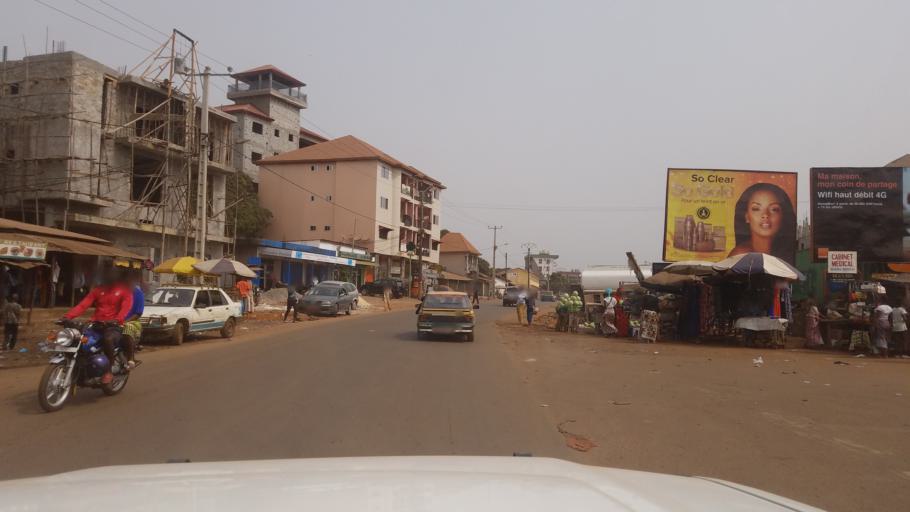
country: GN
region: Conakry
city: Conakry
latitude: 9.6522
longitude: -13.6021
